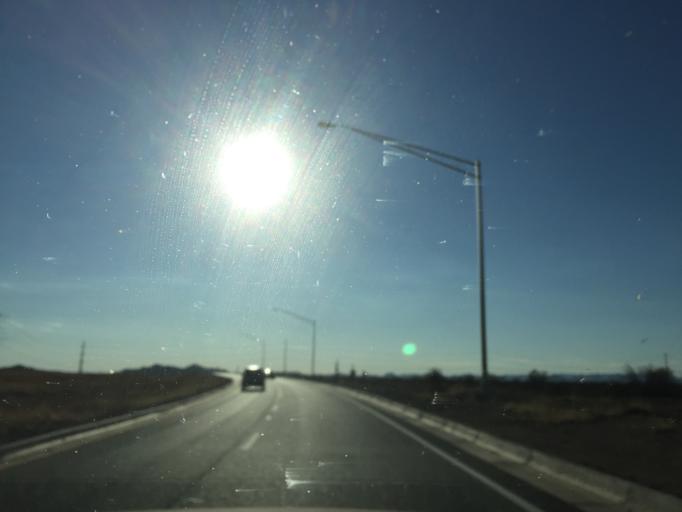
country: US
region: Arizona
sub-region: Maricopa County
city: Anthem
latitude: 33.7698
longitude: -112.1339
